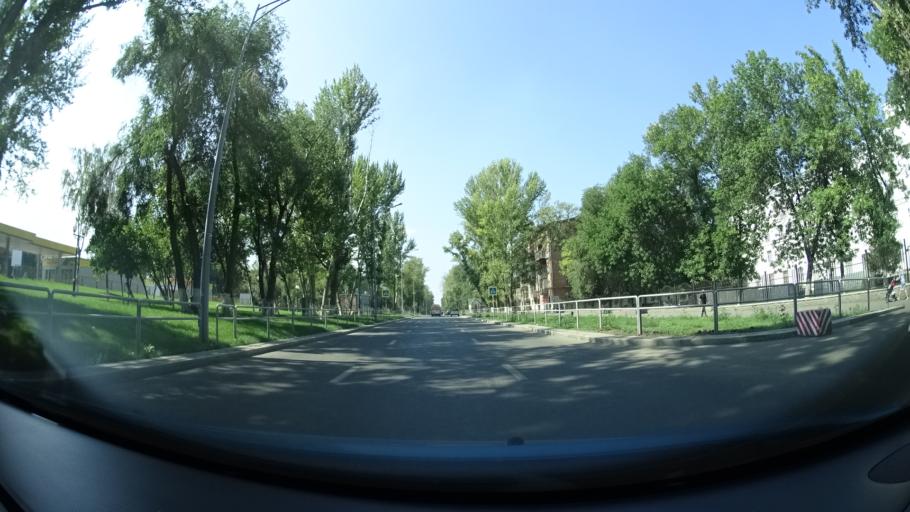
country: RU
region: Samara
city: Samara
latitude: 53.2091
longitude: 50.1719
